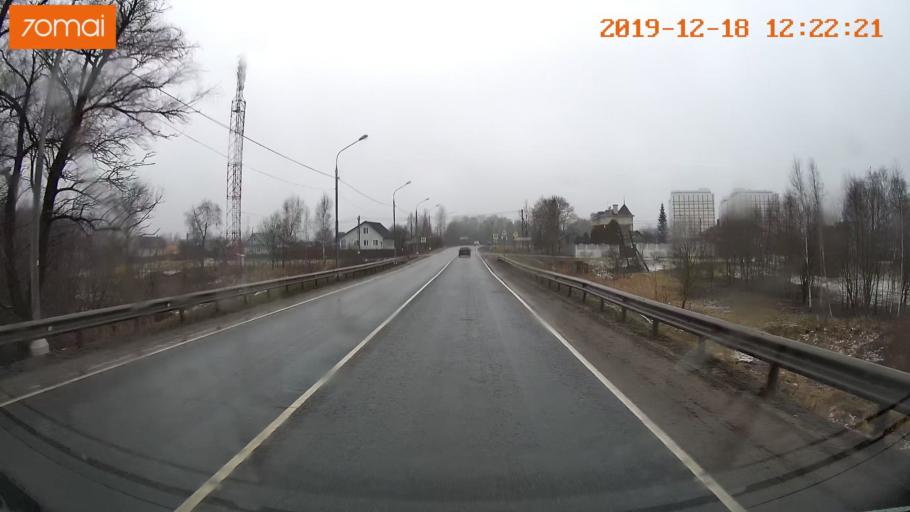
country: RU
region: Moskovskaya
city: Novopetrovskoye
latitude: 56.0050
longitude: 36.4798
